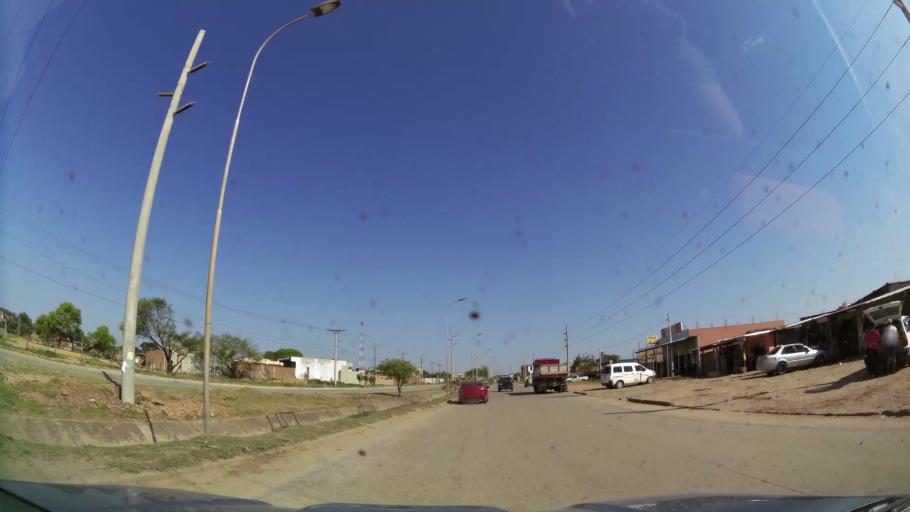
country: BO
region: Santa Cruz
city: Cotoca
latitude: -17.7775
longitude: -63.1077
